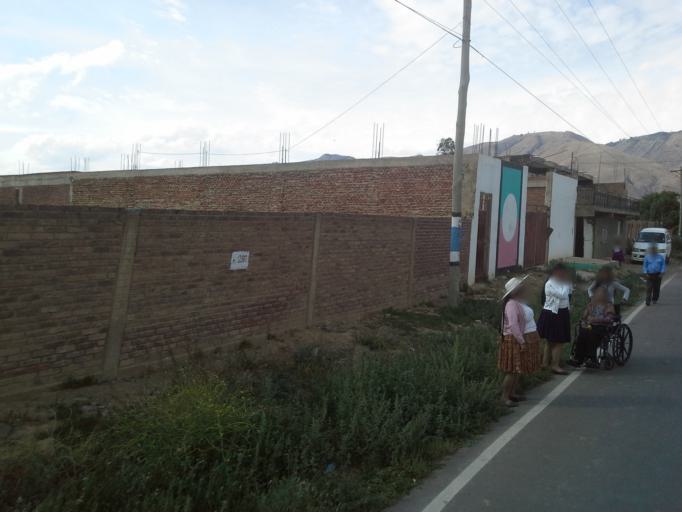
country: BO
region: Cochabamba
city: Tarata
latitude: -17.5624
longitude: -66.0091
